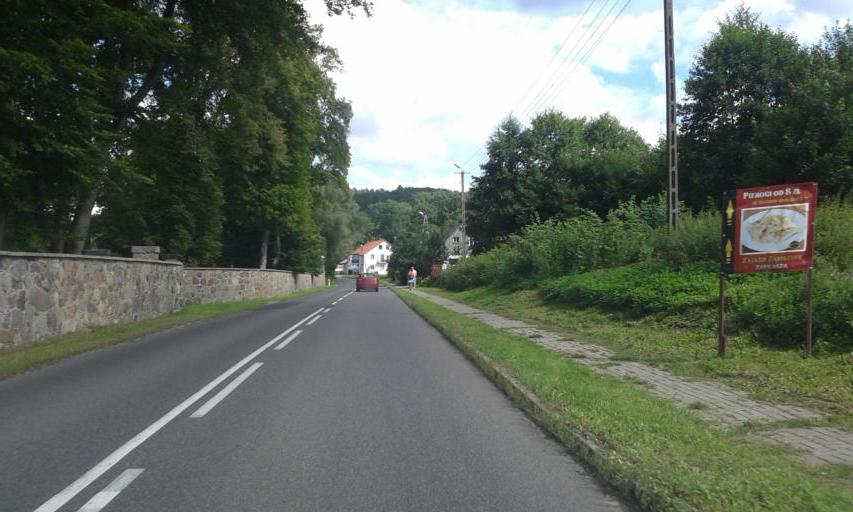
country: PL
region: West Pomeranian Voivodeship
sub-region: Powiat koszalinski
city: Polanow
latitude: 54.2137
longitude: 16.7013
